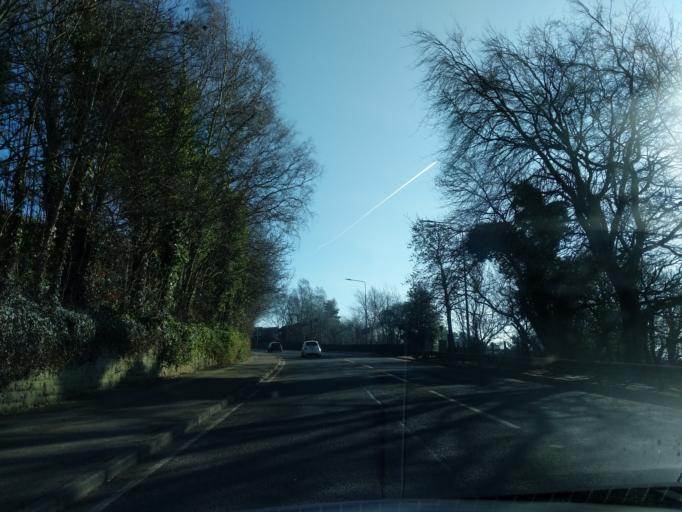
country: GB
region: Scotland
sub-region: South Lanarkshire
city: Lanark
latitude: 55.6762
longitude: -3.7944
